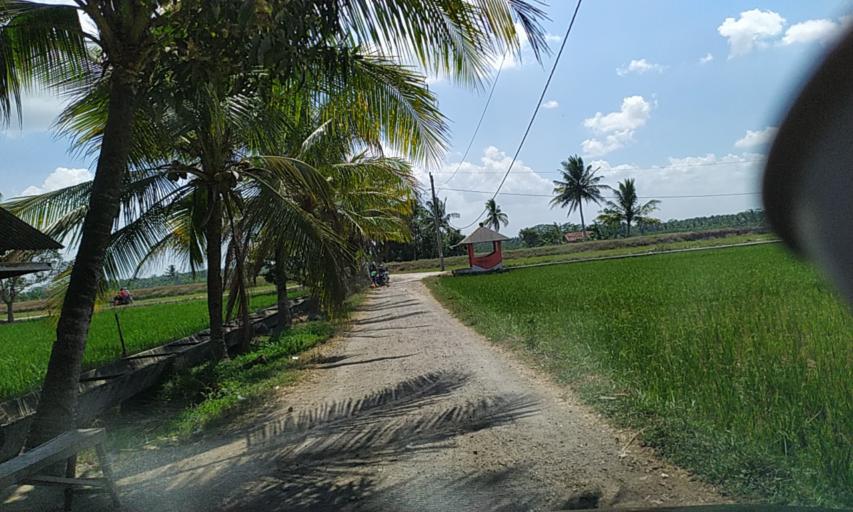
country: ID
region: Central Java
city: Cimrutu
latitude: -7.6102
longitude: 108.7955
